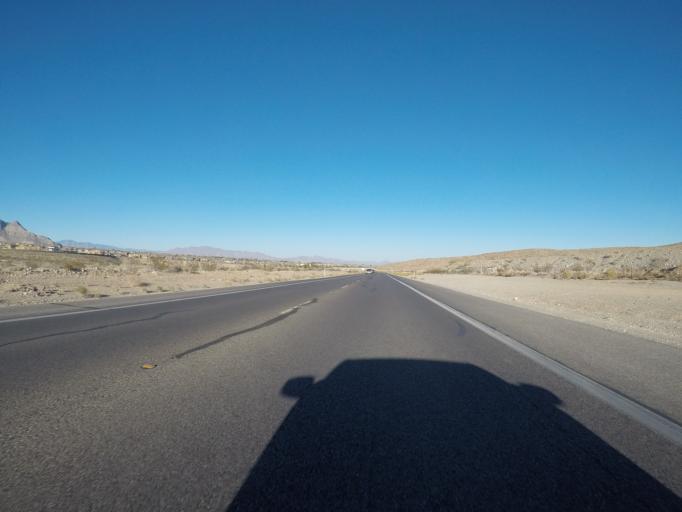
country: US
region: Nevada
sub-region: Clark County
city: Summerlin South
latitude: 36.1518
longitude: -115.3686
